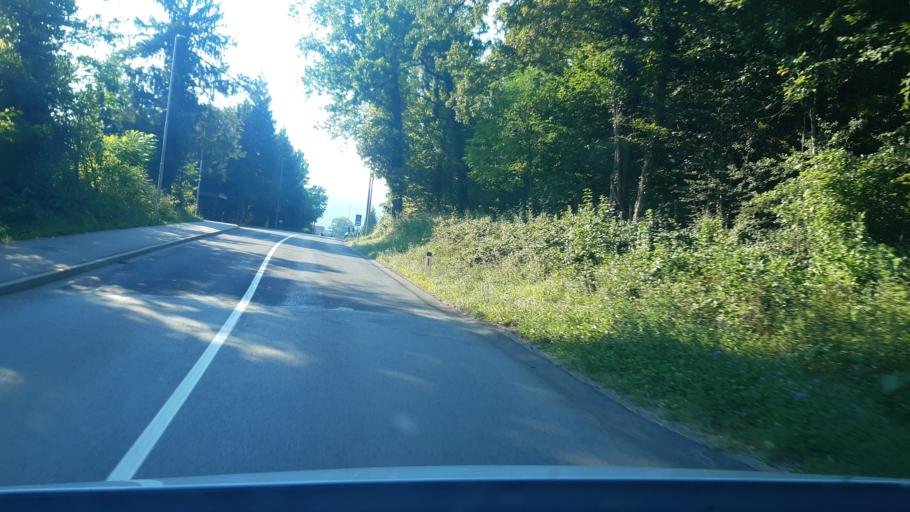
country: SI
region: Crnomelj
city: Crnomelj
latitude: 45.5882
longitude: 15.1813
